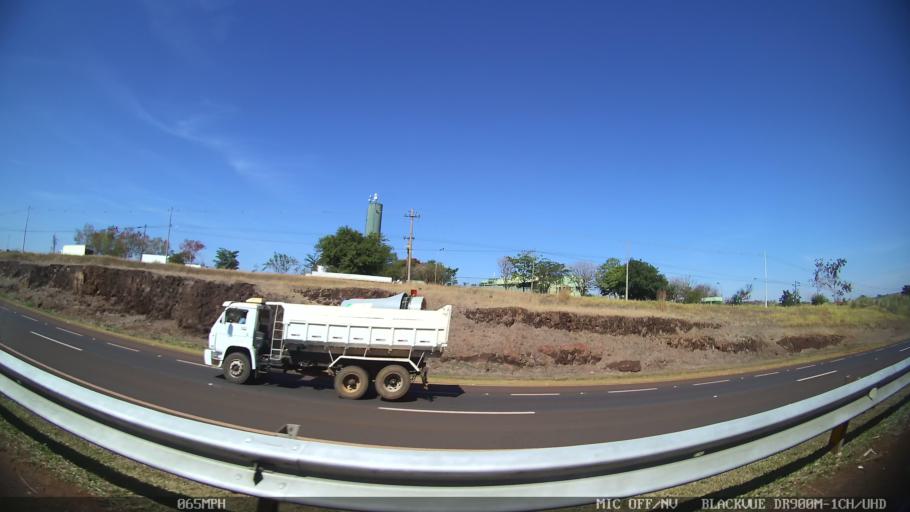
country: BR
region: Sao Paulo
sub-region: Ribeirao Preto
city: Ribeirao Preto
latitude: -21.1356
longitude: -47.8597
